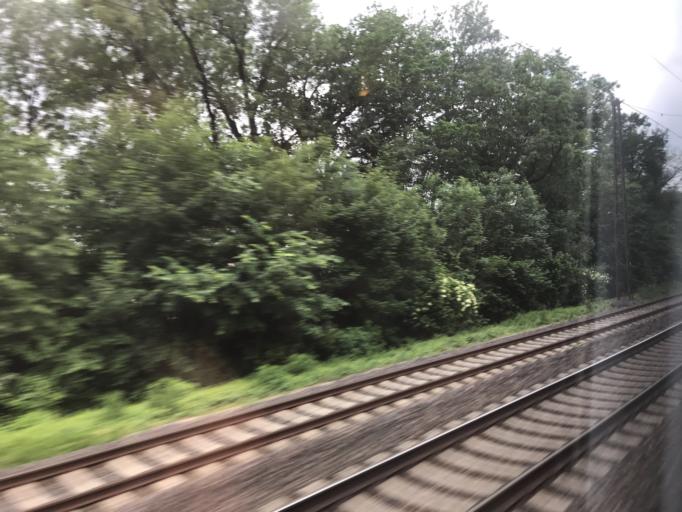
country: DE
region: Bavaria
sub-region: Swabia
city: Guenzburg
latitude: 48.4591
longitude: 10.2735
